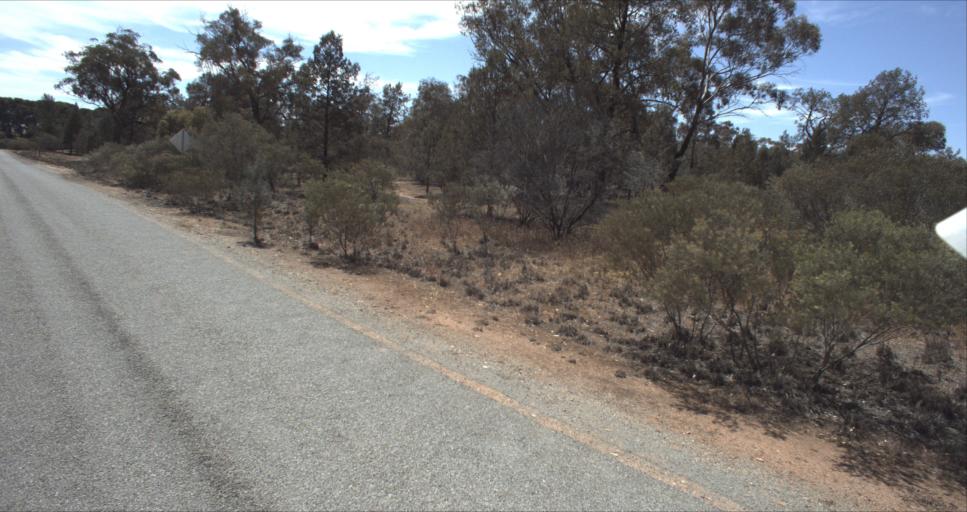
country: AU
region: New South Wales
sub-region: Leeton
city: Leeton
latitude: -34.6723
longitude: 146.4441
